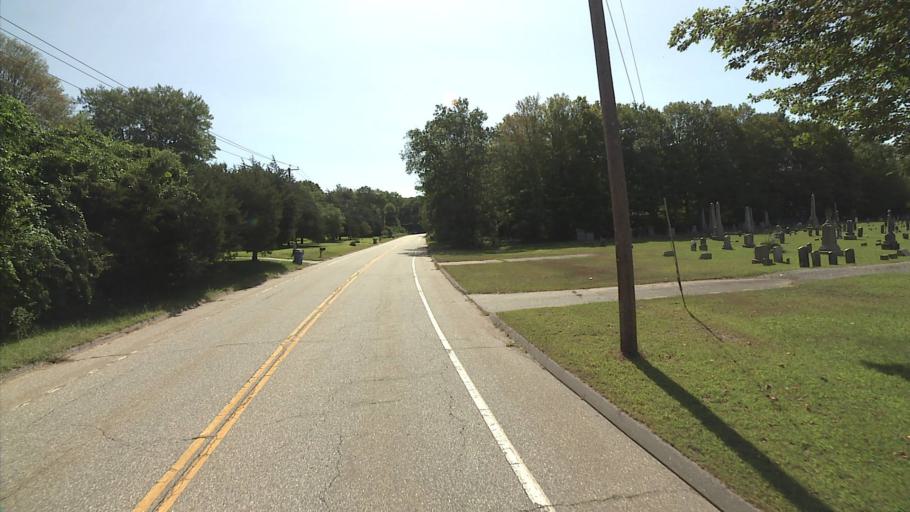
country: US
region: Connecticut
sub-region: New London County
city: Baltic
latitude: 41.6277
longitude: -72.1214
